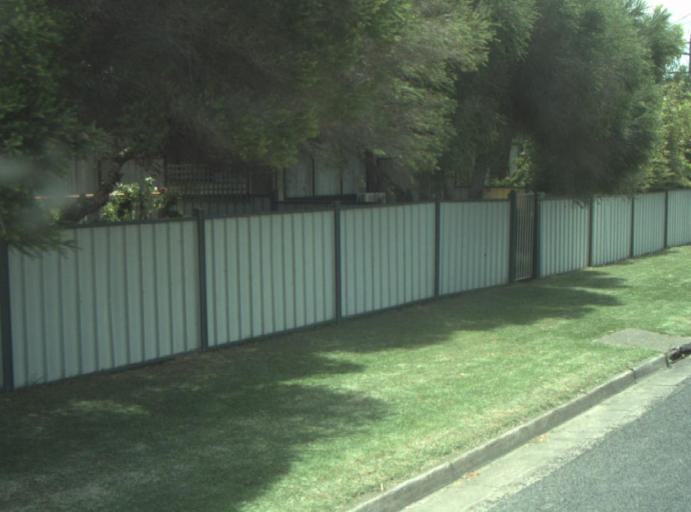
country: AU
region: Victoria
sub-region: Greater Geelong
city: Leopold
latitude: -38.2659
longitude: 144.5149
